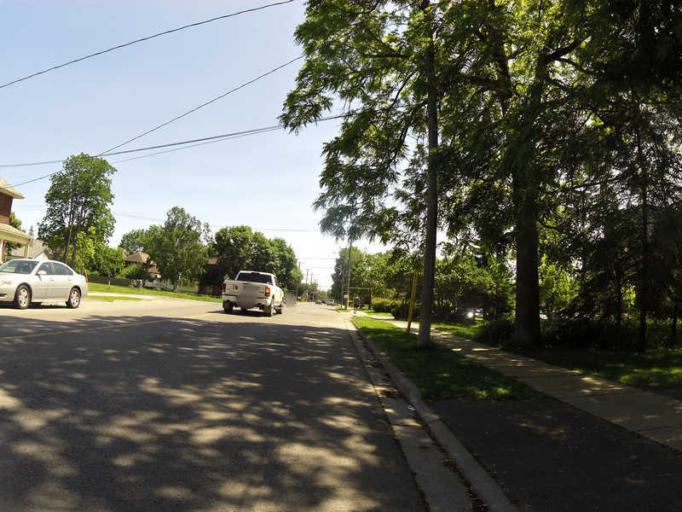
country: CA
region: Ontario
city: Peterborough
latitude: 44.2916
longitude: -78.3166
